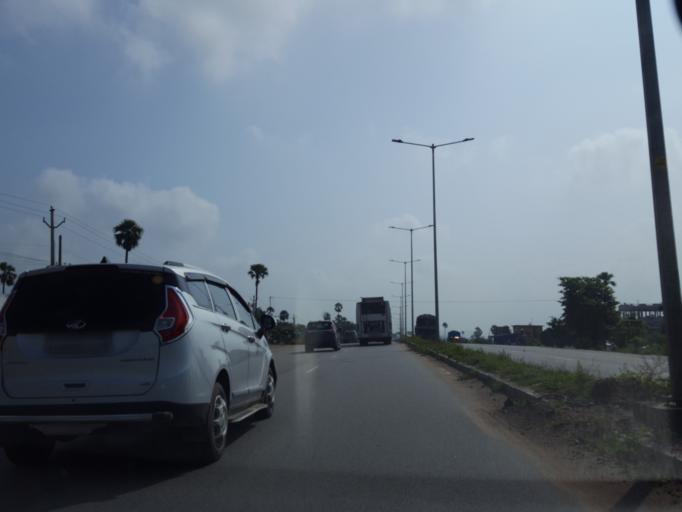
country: IN
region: Telangana
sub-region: Rangareddi
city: Lal Bahadur Nagar
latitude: 17.3094
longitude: 78.6919
